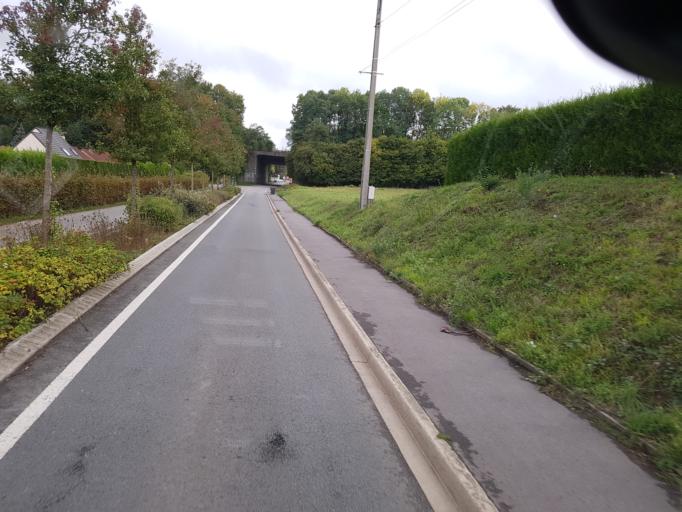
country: FR
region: Nord-Pas-de-Calais
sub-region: Departement du Pas-de-Calais
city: Angres
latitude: 50.4002
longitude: 2.7538
